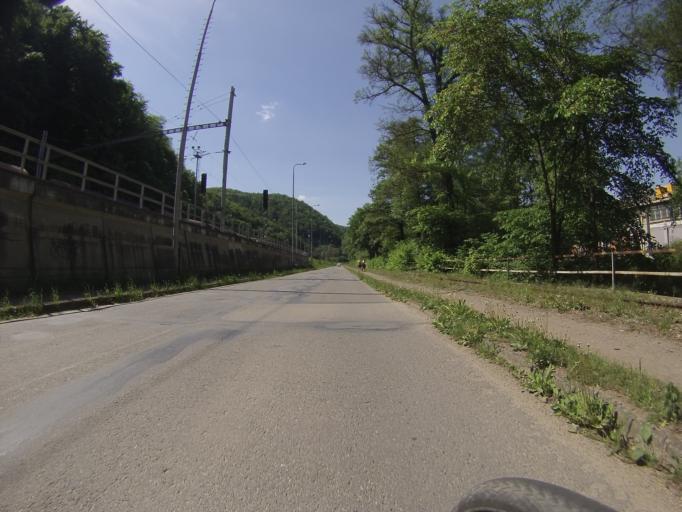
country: CZ
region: South Moravian
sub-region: Okres Blansko
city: Adamov
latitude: 49.2976
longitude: 16.6574
